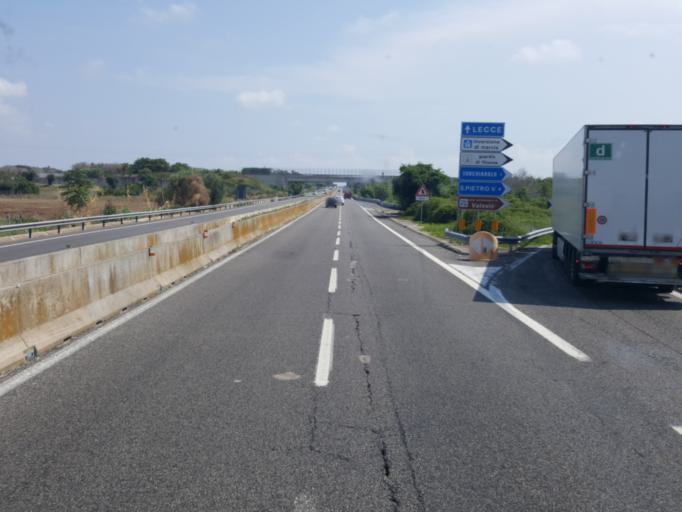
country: IT
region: Apulia
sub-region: Provincia di Brindisi
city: Torchiarolo
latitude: 40.4888
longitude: 18.0392
